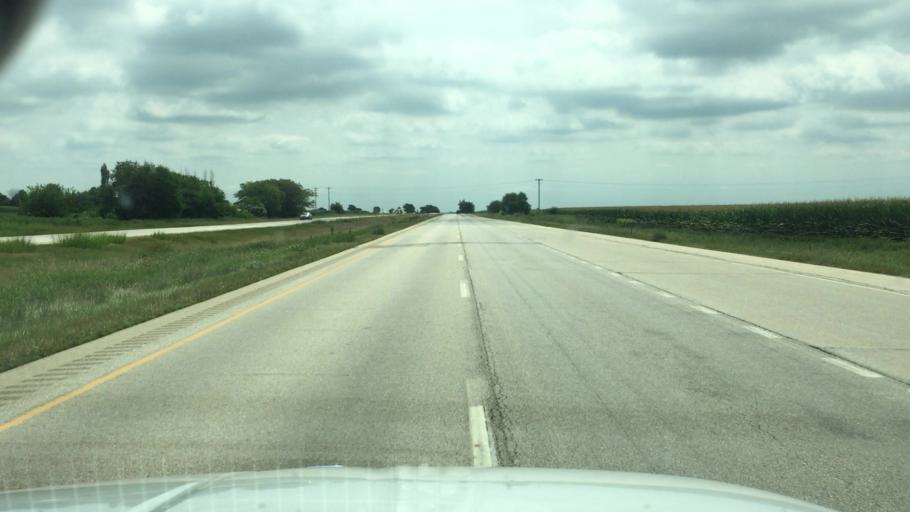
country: US
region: Illinois
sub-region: Knox County
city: Knoxville
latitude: 40.9095
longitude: -90.2456
